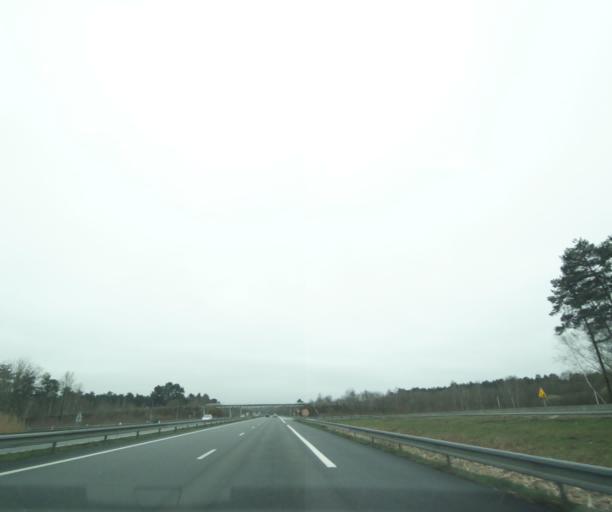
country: FR
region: Centre
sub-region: Departement du Loir-et-Cher
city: Theillay
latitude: 47.3470
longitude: 2.0489
